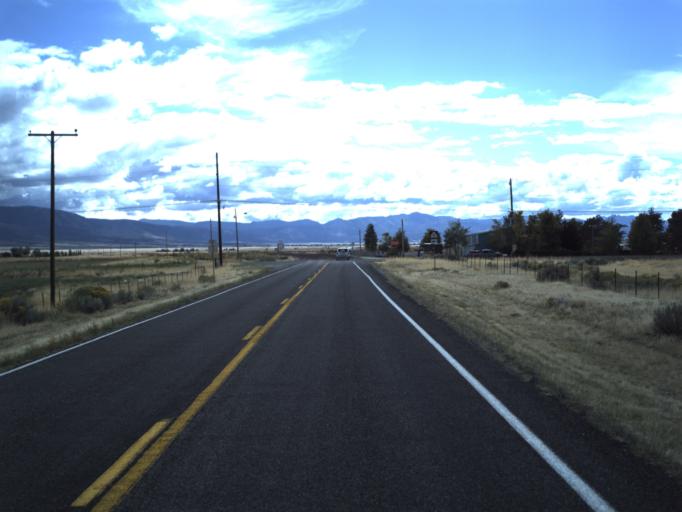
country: US
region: Utah
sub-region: Millard County
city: Fillmore
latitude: 38.9806
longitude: -112.4099
